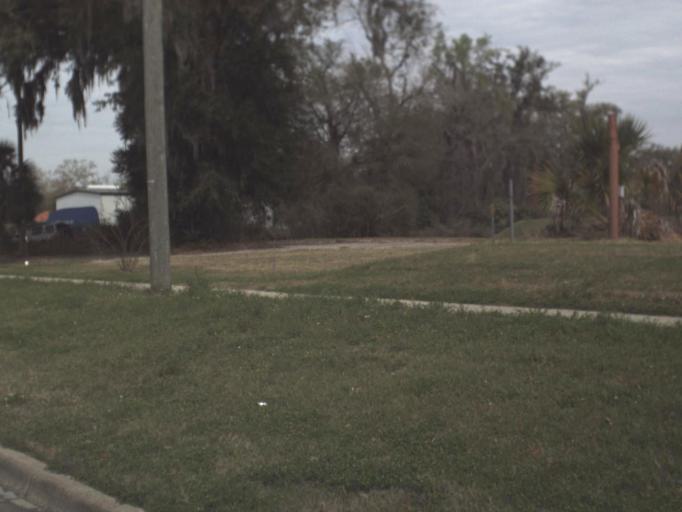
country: US
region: Florida
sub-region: Leon County
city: Tallahassee
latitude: 30.4540
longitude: -84.3399
